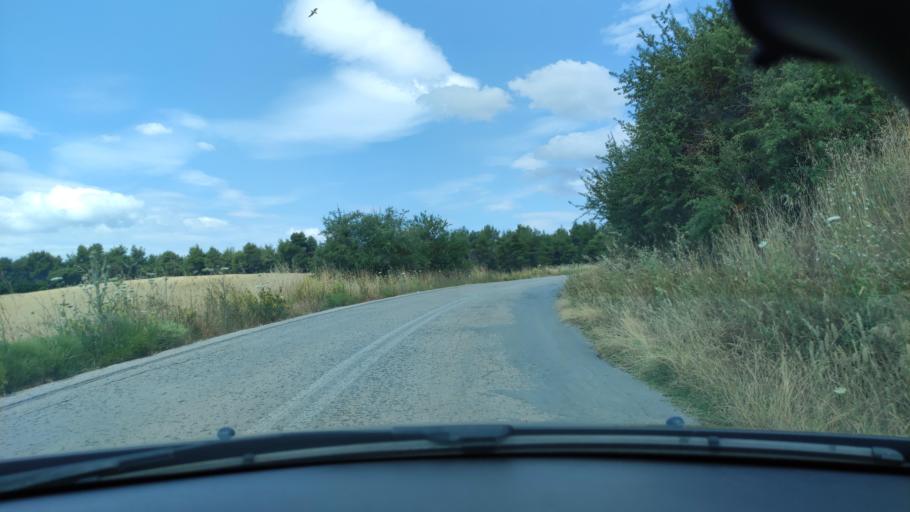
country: GR
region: Central Greece
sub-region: Nomos Evvoias
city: Afration
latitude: 38.5201
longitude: 23.7483
